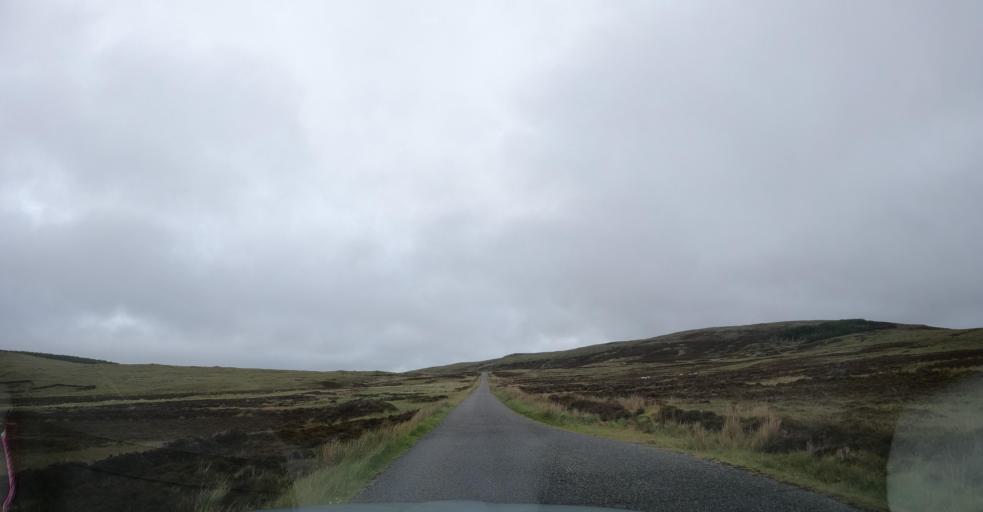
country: GB
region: Scotland
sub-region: Eilean Siar
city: Isle of North Uist
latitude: 57.6064
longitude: -7.3777
